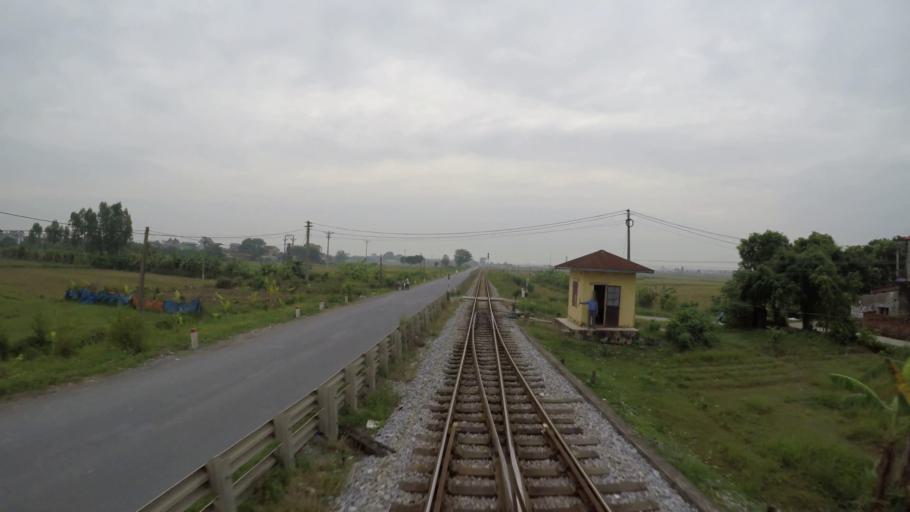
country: VN
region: Hung Yen
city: Ban Yen Nhan
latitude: 20.9720
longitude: 106.0977
